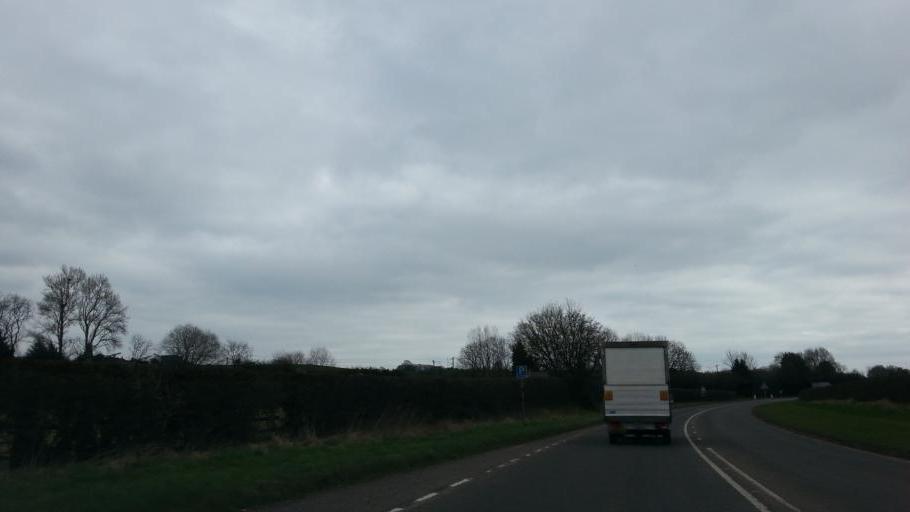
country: GB
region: England
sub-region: Staffordshire
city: Stone
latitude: 52.8877
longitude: -2.1251
